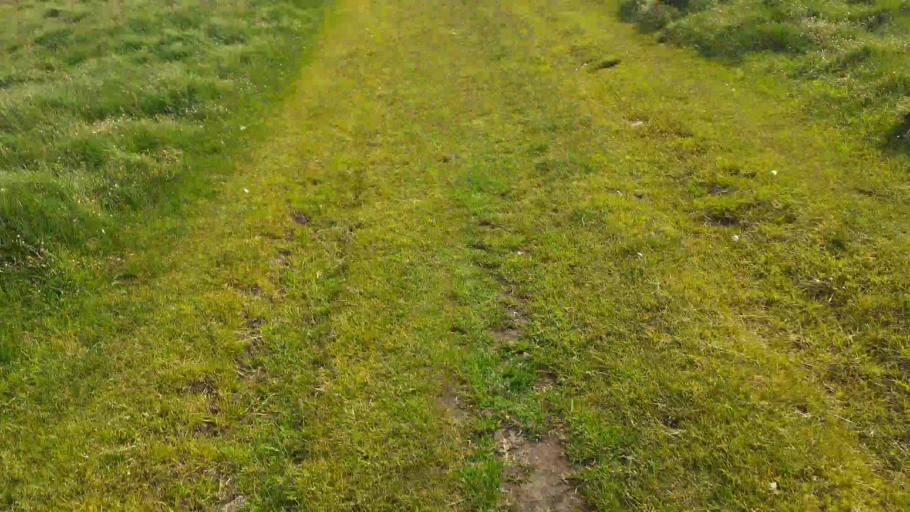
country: IS
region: Northeast
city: Dalvik
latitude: 66.5505
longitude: -17.9928
